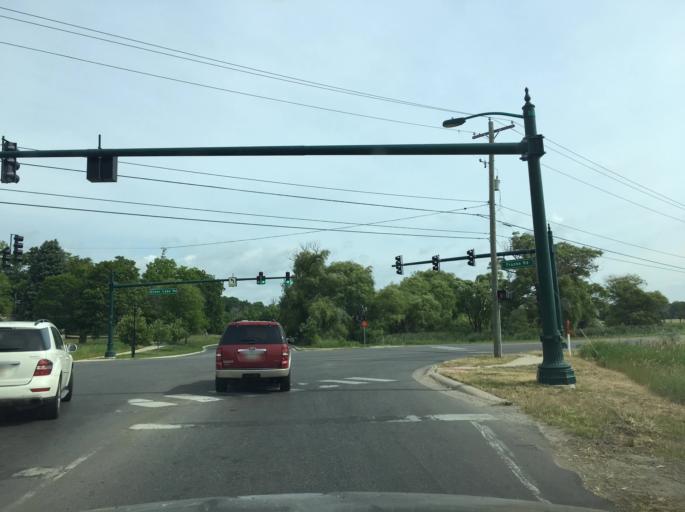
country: US
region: Michigan
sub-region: Grand Traverse County
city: Traverse City
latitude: 44.7472
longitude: -85.6453
